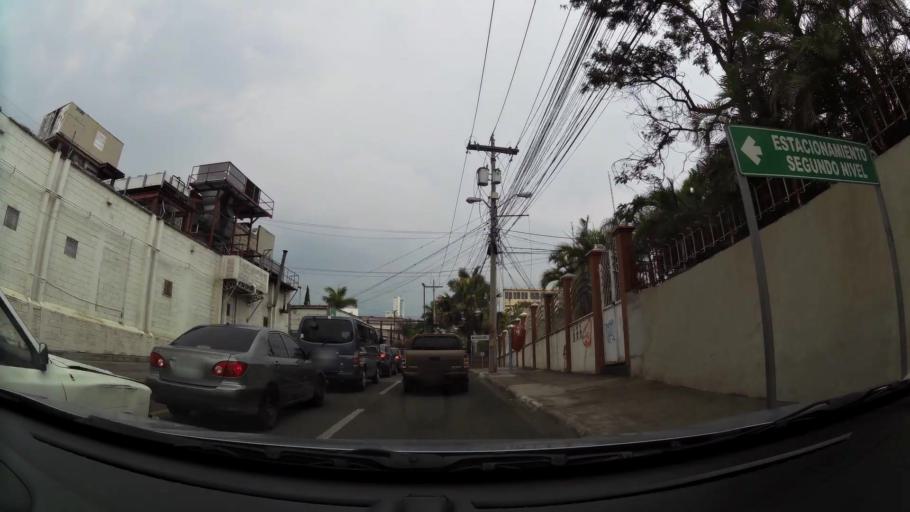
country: HN
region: Francisco Morazan
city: Tegucigalpa
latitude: 14.0872
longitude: -87.1957
